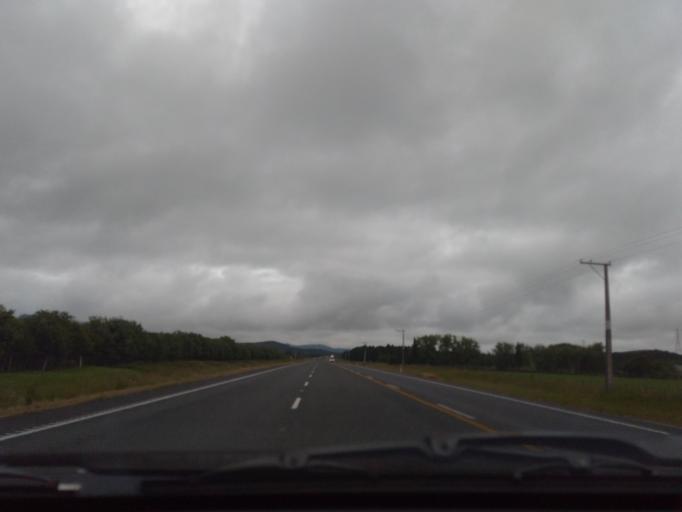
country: NZ
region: Northland
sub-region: Whangarei
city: Ruakaka
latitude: -36.0161
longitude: 174.4184
